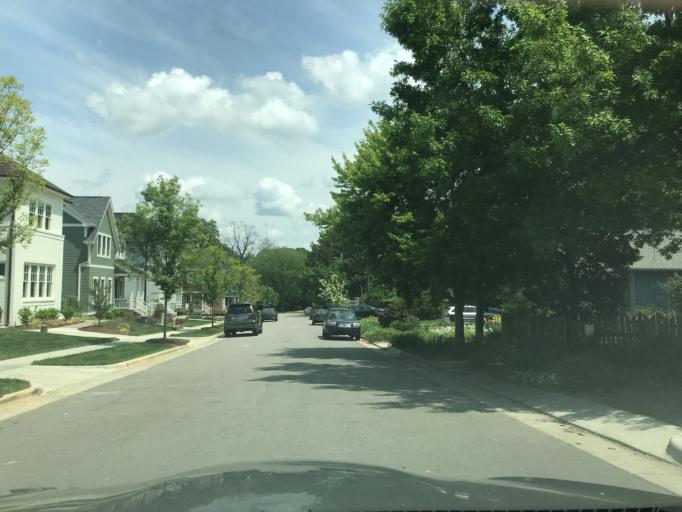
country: US
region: North Carolina
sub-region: Wake County
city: Raleigh
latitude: 35.7916
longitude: -78.6282
